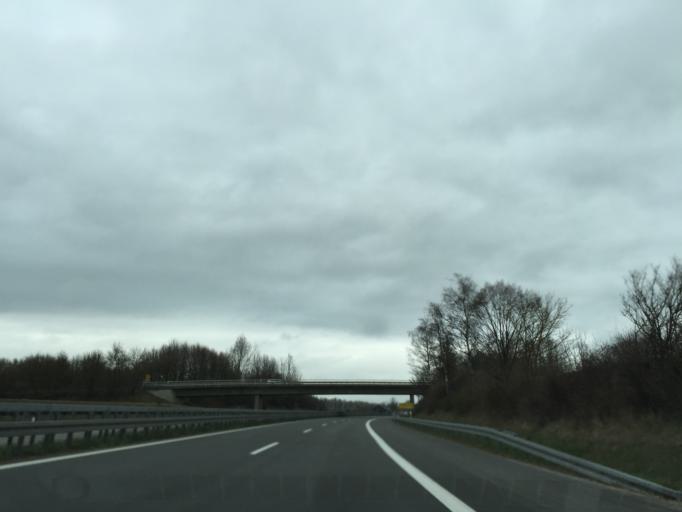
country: DE
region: Baden-Wuerttemberg
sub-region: Freiburg Region
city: Donaueschingen
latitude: 47.9695
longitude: 8.5120
